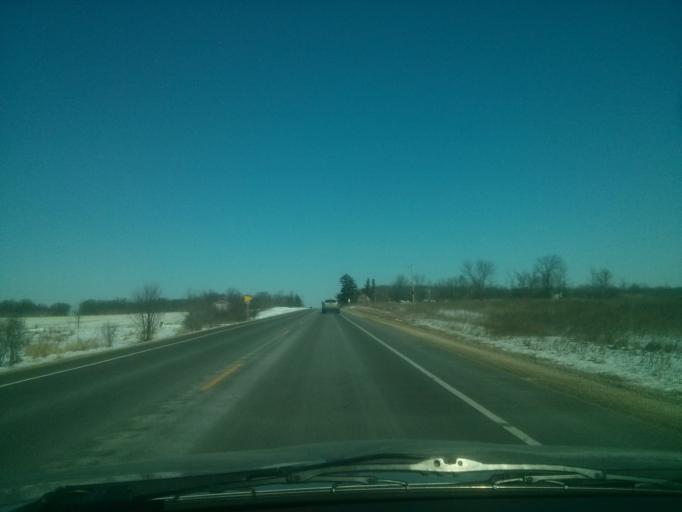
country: US
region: Wisconsin
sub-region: Polk County
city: Clear Lake
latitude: 45.1902
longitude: -92.2834
